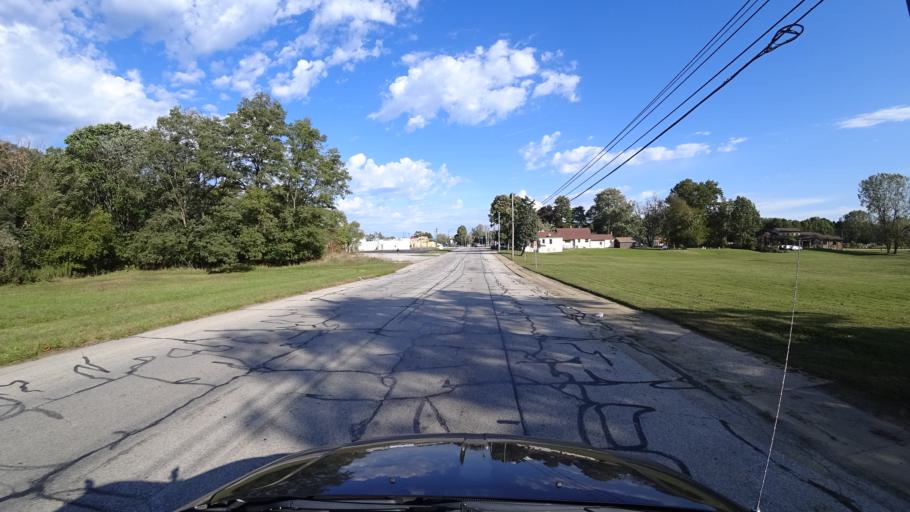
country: US
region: Indiana
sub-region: LaPorte County
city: Trail Creek
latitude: 41.7065
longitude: -86.8697
